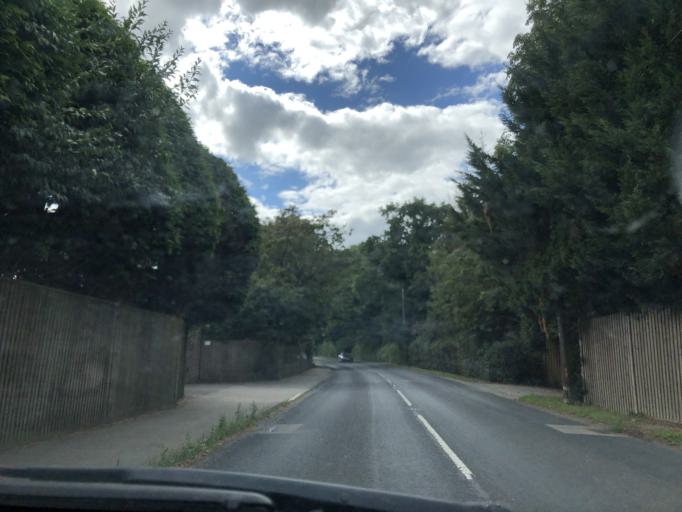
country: GB
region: England
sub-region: Kent
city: Edenbridge
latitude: 51.2219
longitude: 0.0573
